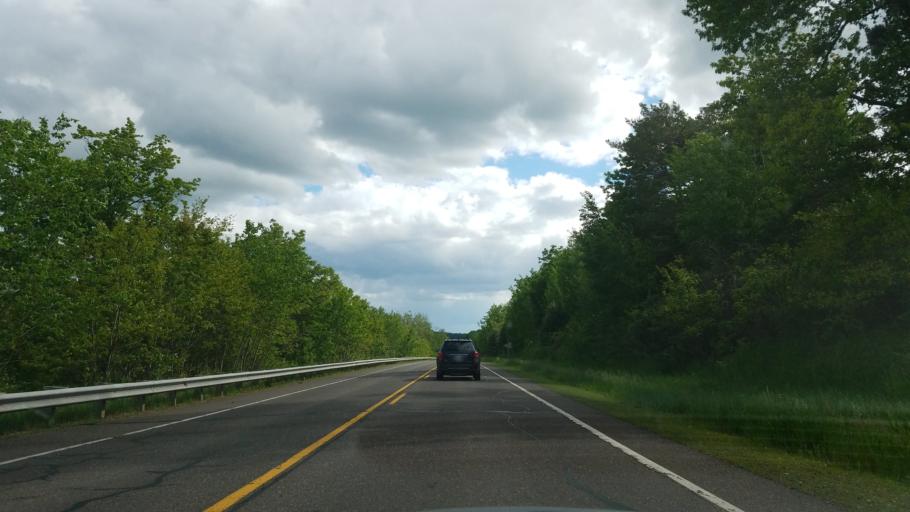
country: US
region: Wisconsin
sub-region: Burnett County
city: Siren
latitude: 46.0953
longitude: -92.2392
